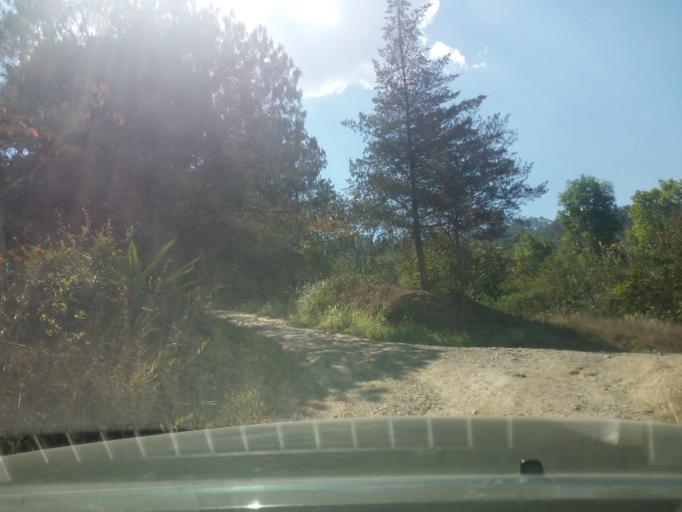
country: CO
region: Boyaca
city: Guateque
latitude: 4.9888
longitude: -73.4650
